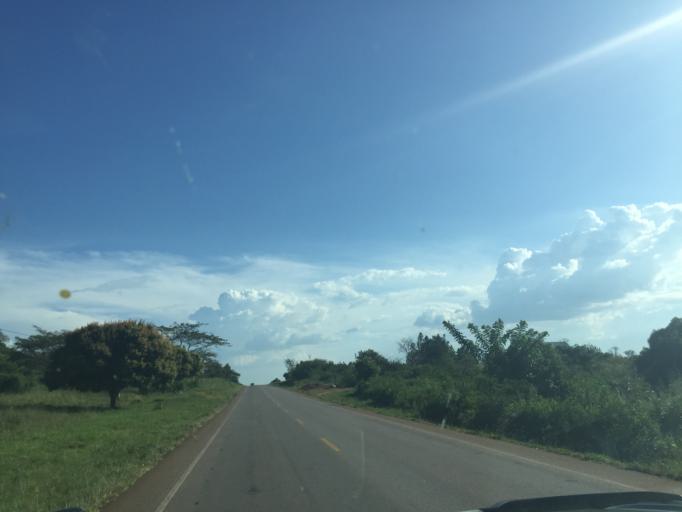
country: UG
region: Central Region
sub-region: Nakasongola District
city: Nakasongola
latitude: 1.3137
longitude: 32.4221
